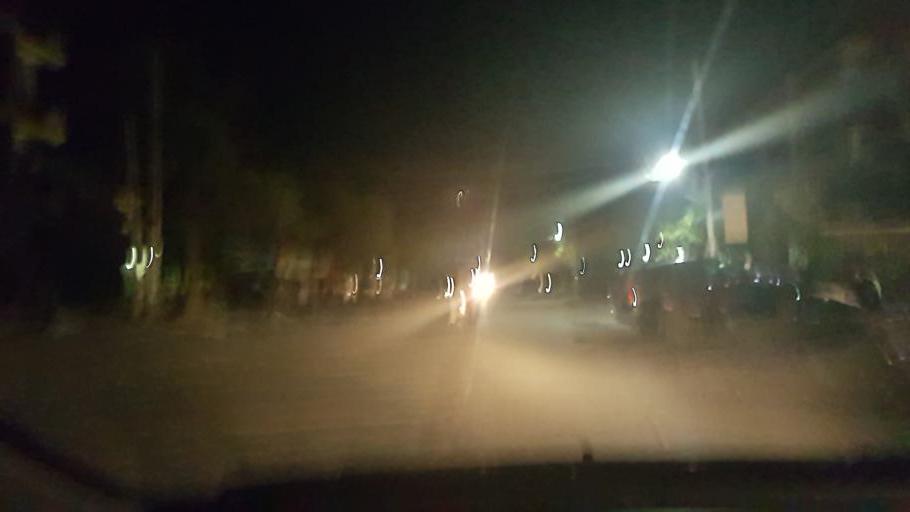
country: MM
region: Mandalay
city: Mandalay
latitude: 21.9795
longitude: 96.0954
